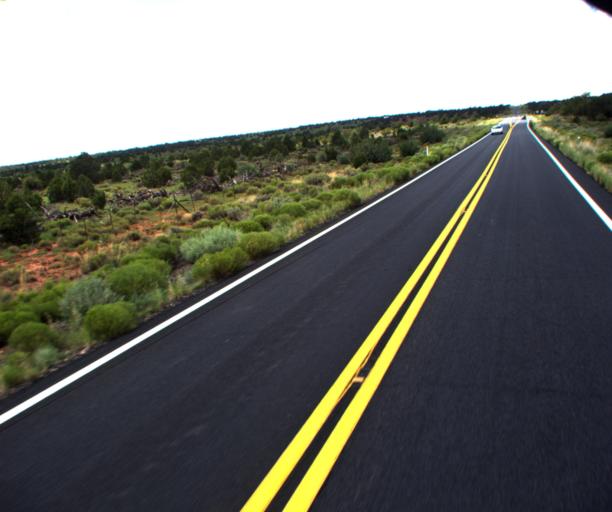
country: US
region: Arizona
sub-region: Coconino County
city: Parks
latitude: 35.6033
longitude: -112.0362
